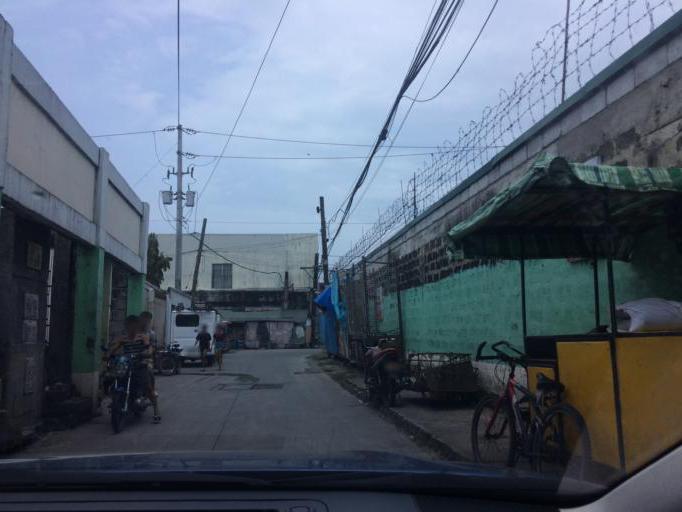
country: PH
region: Metro Manila
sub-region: Makati City
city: Makati City
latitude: 14.5340
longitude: 121.0031
